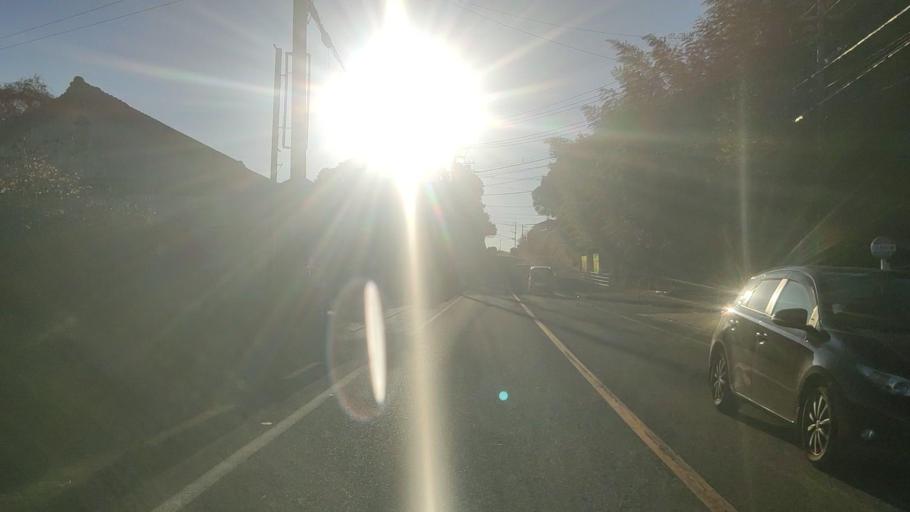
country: JP
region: Miyazaki
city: Miyazaki-shi
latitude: 31.8552
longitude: 131.3631
